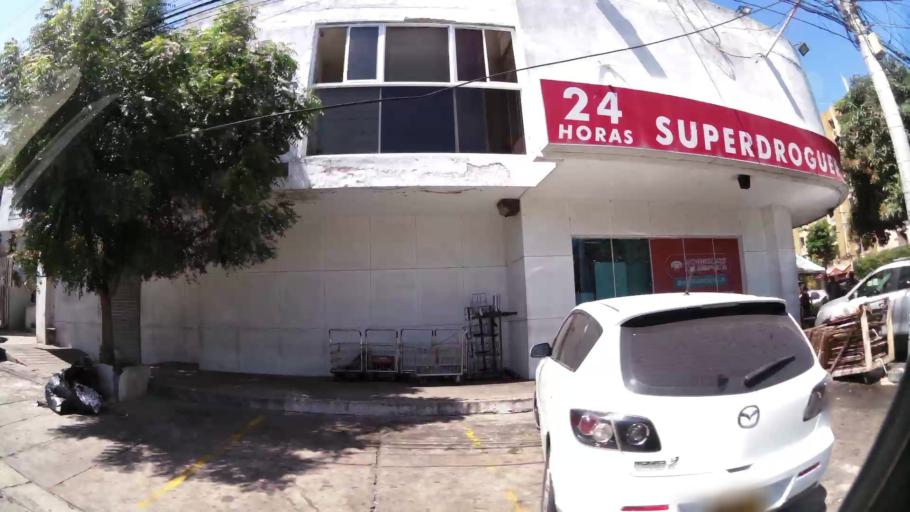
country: CO
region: Atlantico
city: Barranquilla
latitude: 10.9917
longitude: -74.8079
